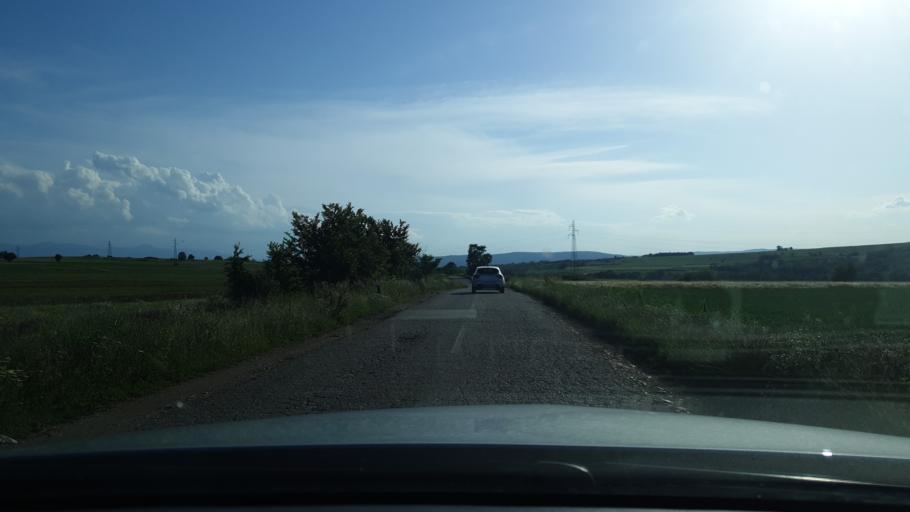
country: RS
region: Central Serbia
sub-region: Nisavski Okrug
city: Aleksinac
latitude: 43.6133
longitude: 21.6603
